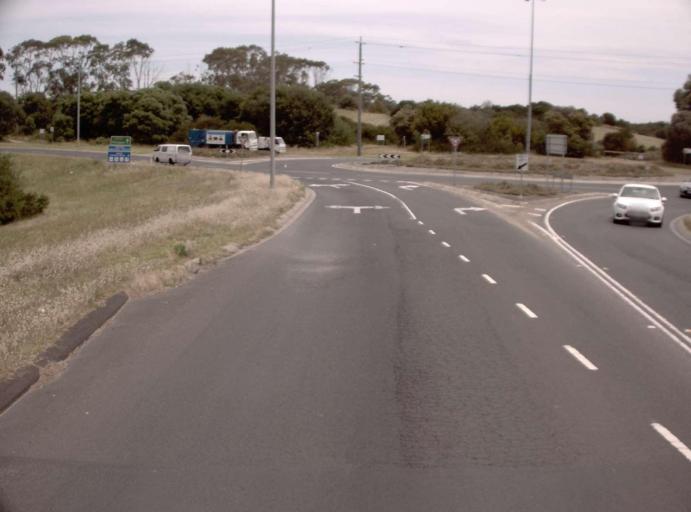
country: AU
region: Victoria
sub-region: Mornington Peninsula
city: Rosebud West
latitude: -38.3765
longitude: 144.8899
